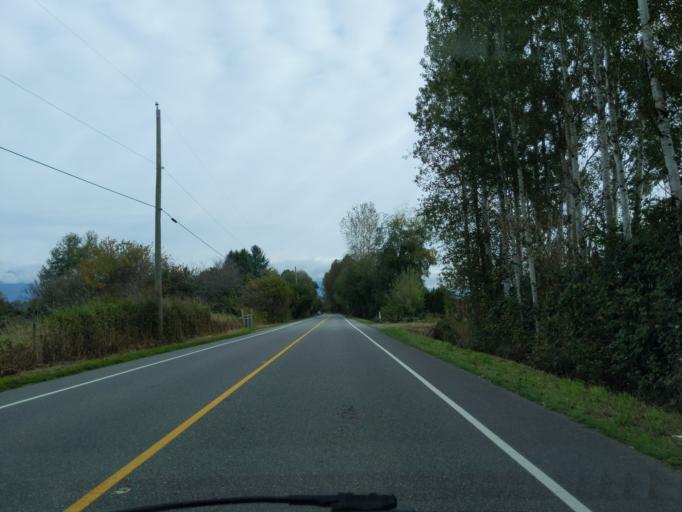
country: CA
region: British Columbia
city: Walnut Grove
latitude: 49.2006
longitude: -122.6345
